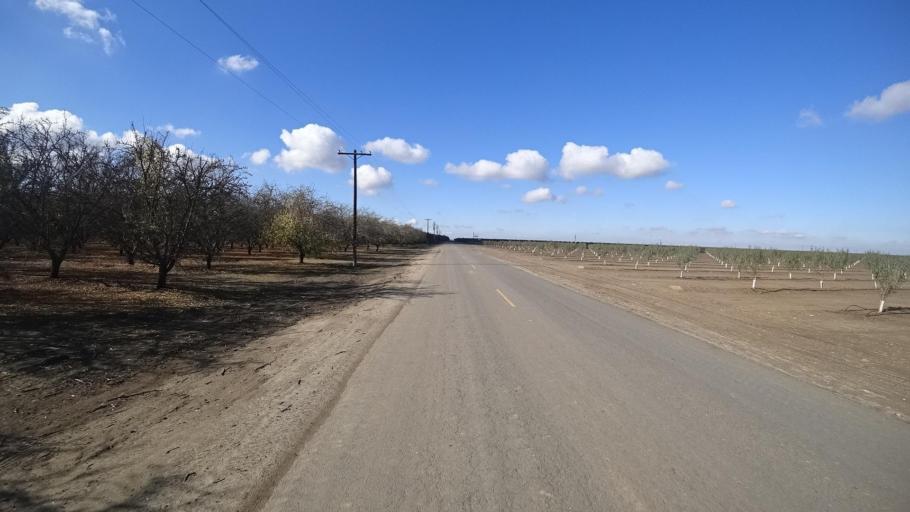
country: US
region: California
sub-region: Kern County
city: McFarland
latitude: 35.6598
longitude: -119.2552
